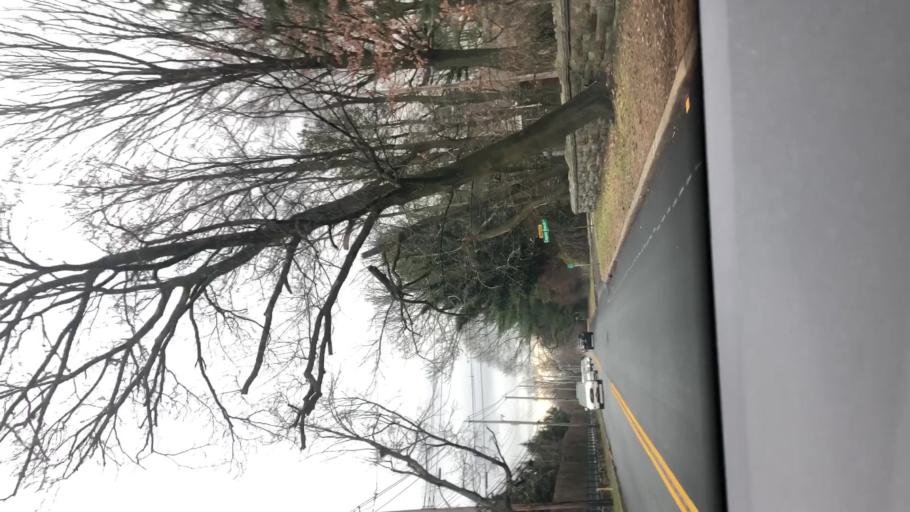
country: US
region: New York
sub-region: Westchester County
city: Larchmont
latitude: 40.9608
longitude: -73.7725
